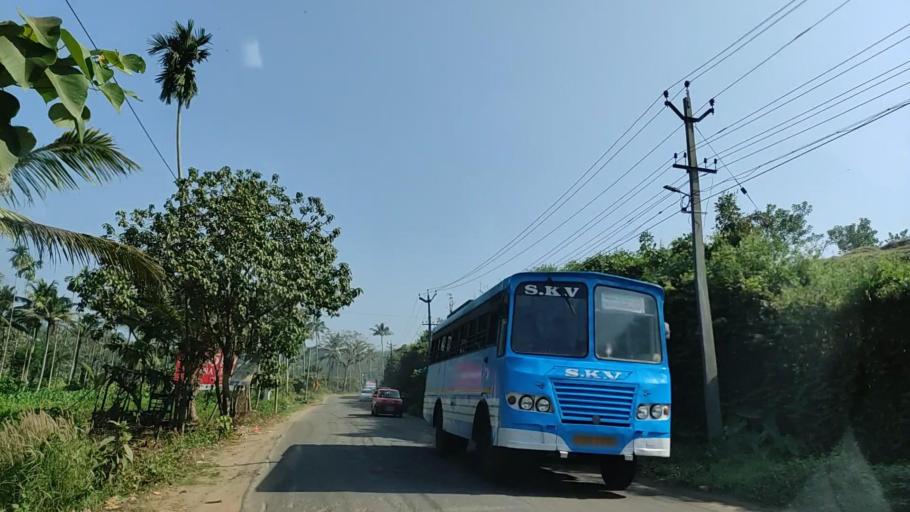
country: IN
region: Kerala
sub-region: Kollam
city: Punalur
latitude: 8.9119
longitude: 76.8826
